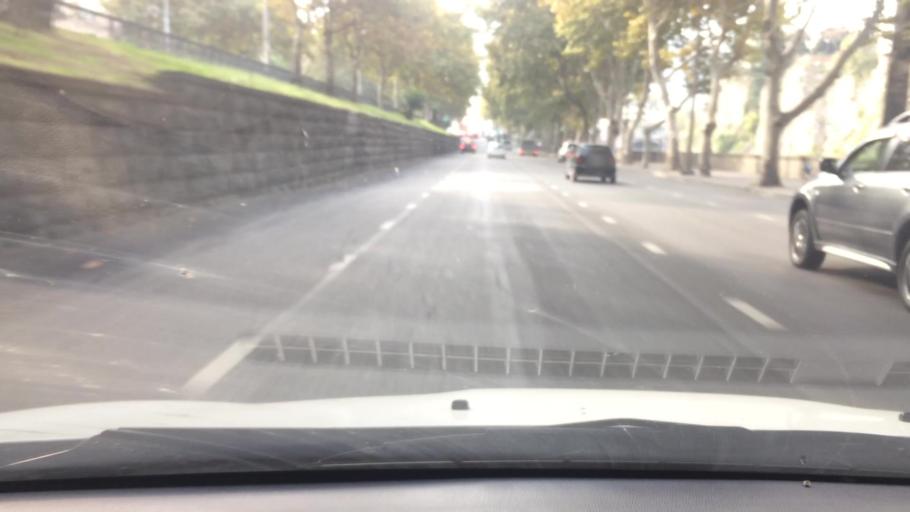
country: GE
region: T'bilisi
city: Tbilisi
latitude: 41.6889
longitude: 44.8146
